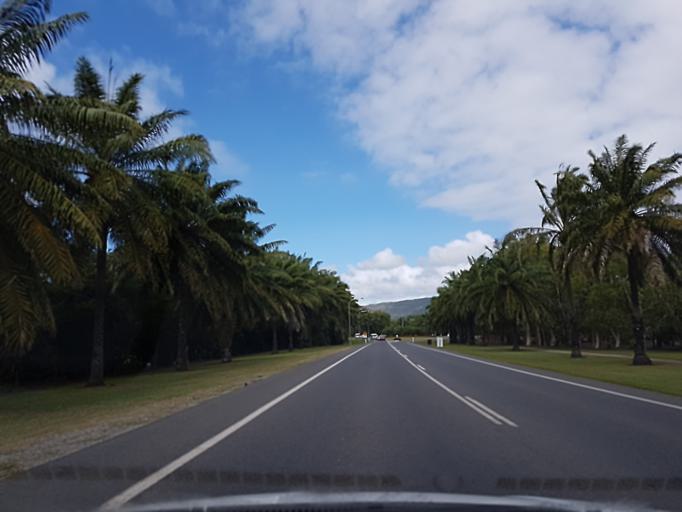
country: AU
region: Queensland
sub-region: Cairns
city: Port Douglas
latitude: -16.5040
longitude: 145.4633
